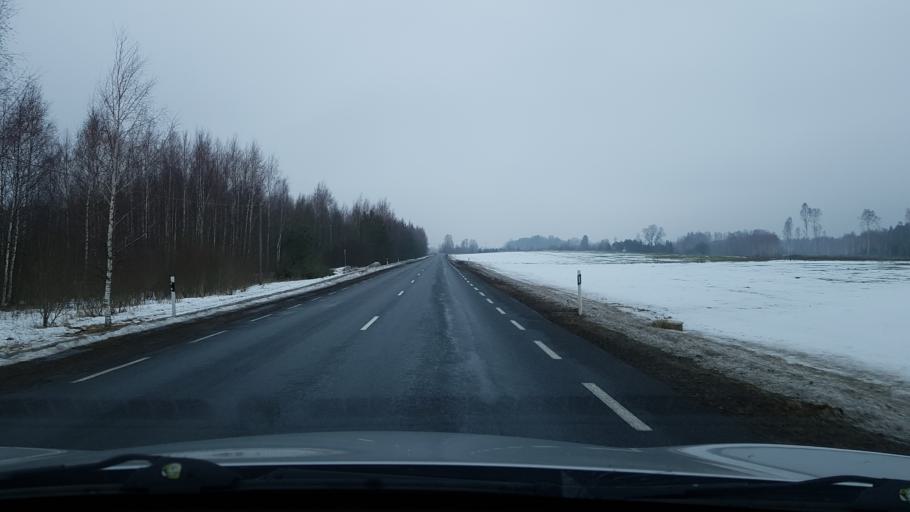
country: EE
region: Valgamaa
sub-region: Torva linn
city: Torva
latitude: 58.1292
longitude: 25.9921
